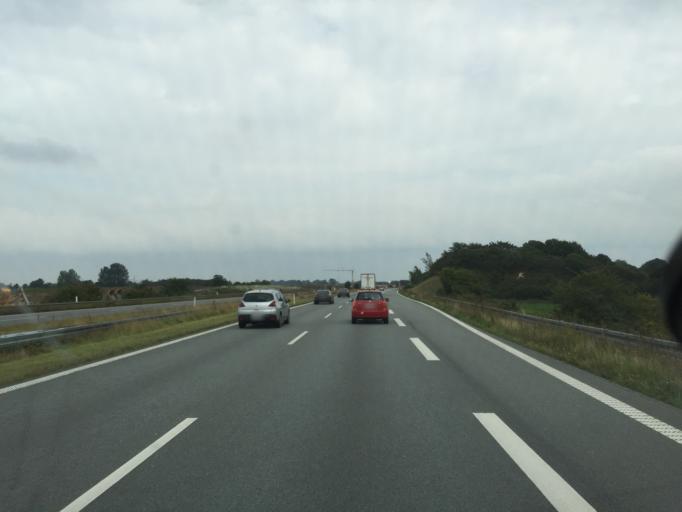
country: DK
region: Zealand
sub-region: Koge Kommune
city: Ejby
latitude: 55.4765
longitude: 12.0898
